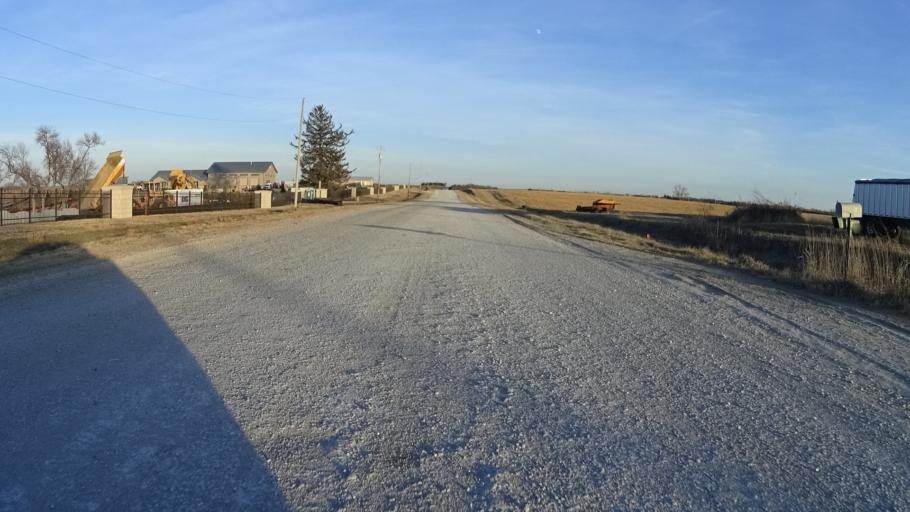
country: US
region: Nebraska
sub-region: Sarpy County
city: Springfield
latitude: 41.1325
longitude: -96.1310
